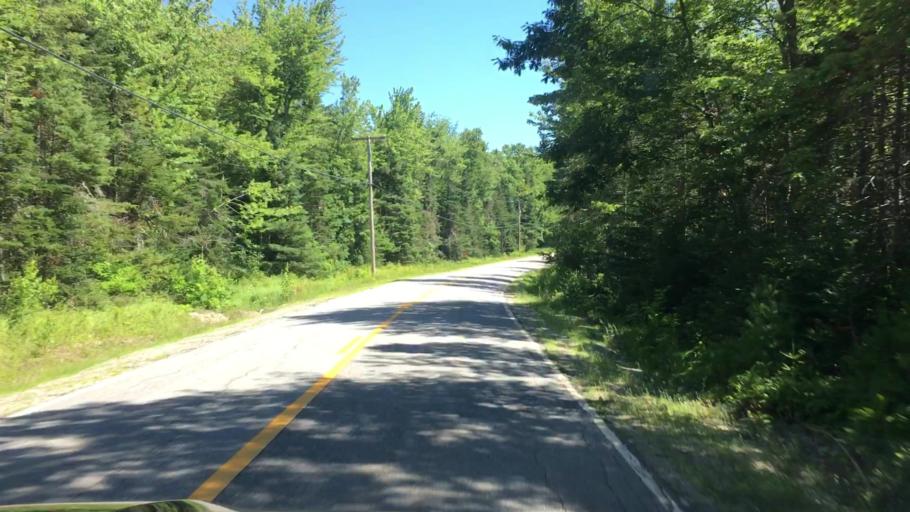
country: US
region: Maine
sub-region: Hancock County
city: Penobscot
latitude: 44.4724
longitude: -68.7013
